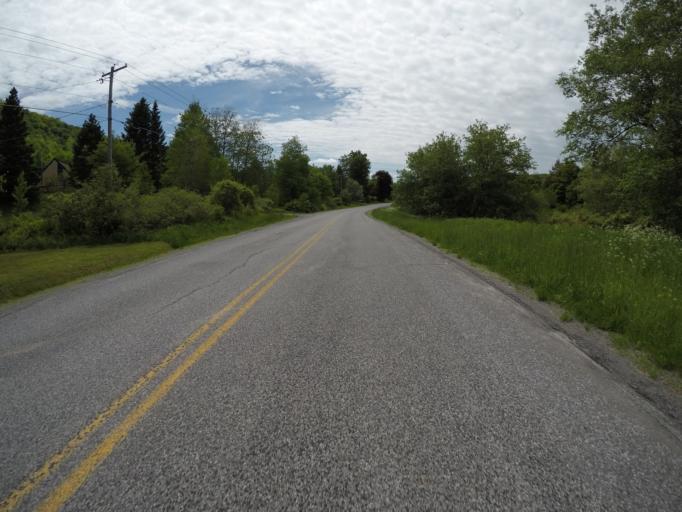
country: US
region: New York
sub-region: Delaware County
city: Stamford
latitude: 42.2350
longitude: -74.5579
